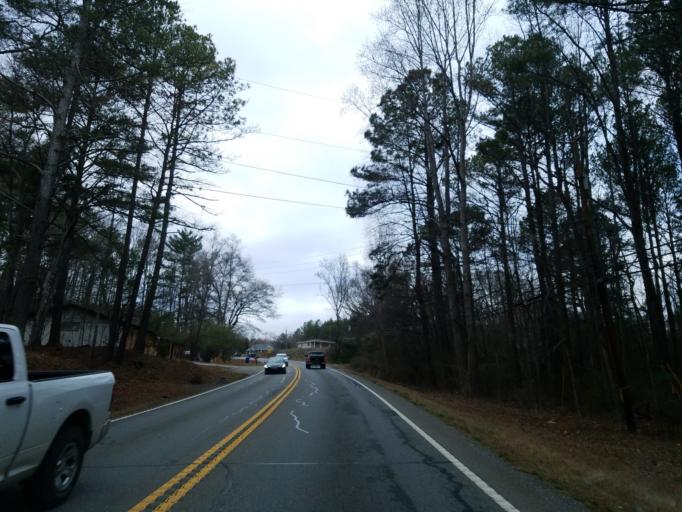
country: US
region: Georgia
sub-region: Cherokee County
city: Canton
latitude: 34.2685
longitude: -84.4955
